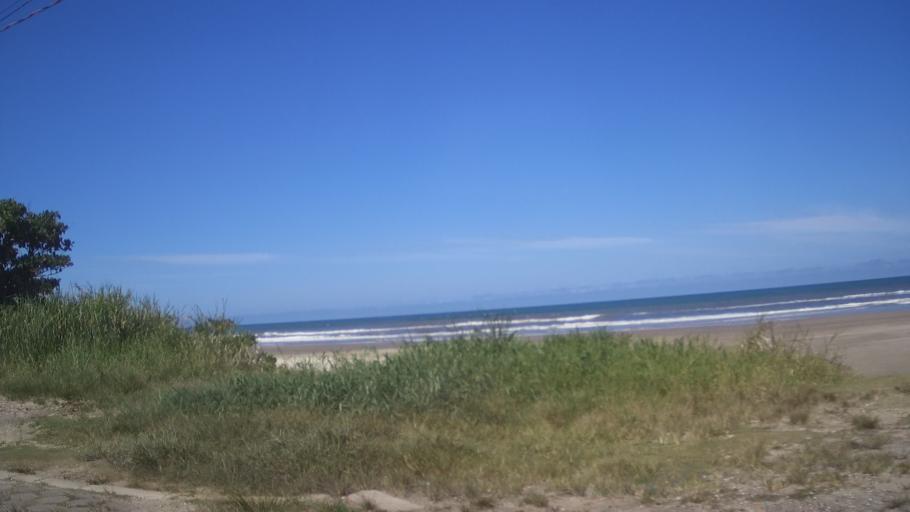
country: BR
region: Sao Paulo
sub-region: Itanhaem
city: Itanhaem
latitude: -24.1532
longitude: -46.7280
